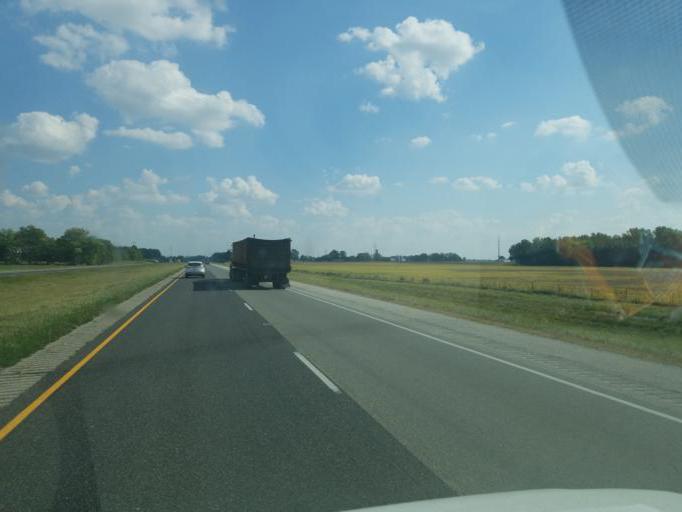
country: US
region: Indiana
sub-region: Allen County
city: Monroeville
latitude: 41.0309
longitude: -84.9028
